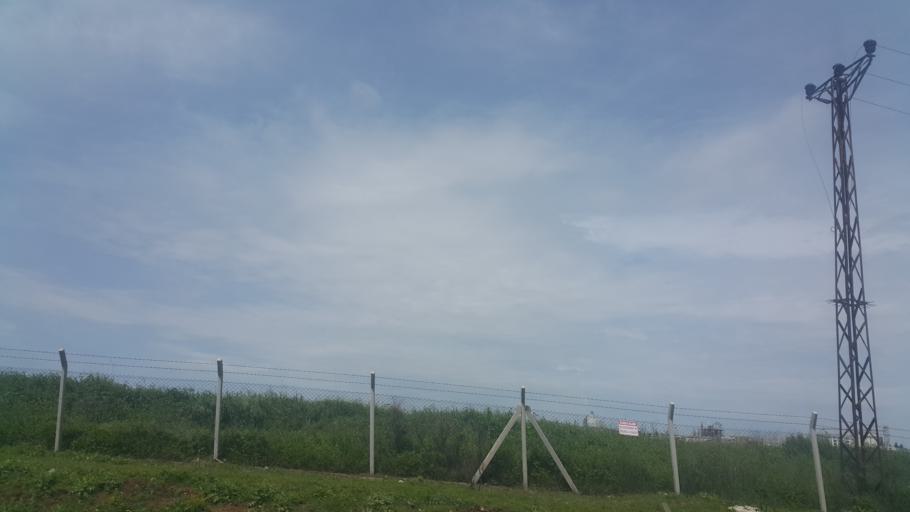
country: TR
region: Adana
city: Yakapinar
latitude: 36.9652
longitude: 35.6182
